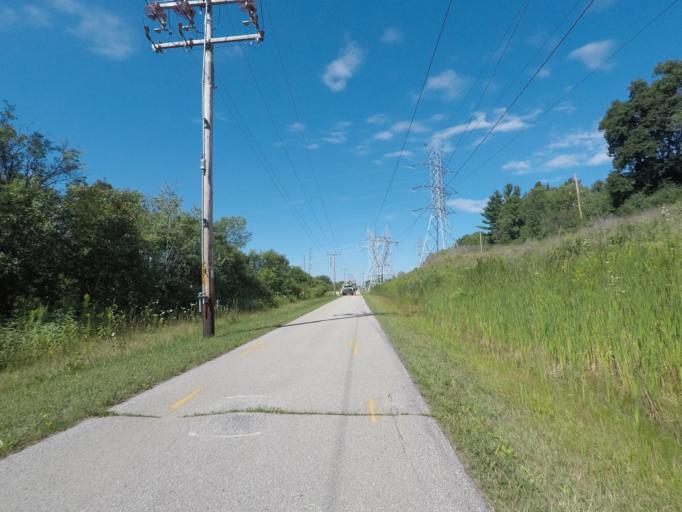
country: US
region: Wisconsin
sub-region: Waukesha County
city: Waukesha
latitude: 43.0099
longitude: -88.1710
